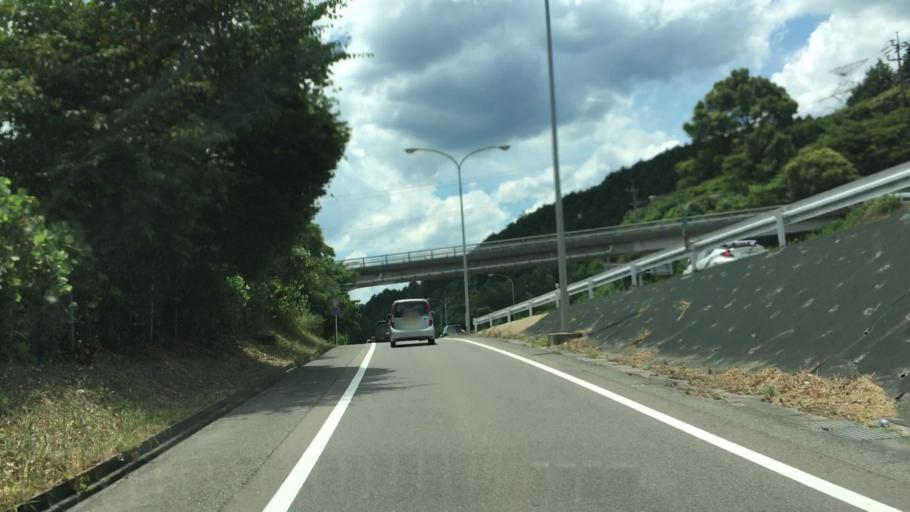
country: JP
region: Fukuoka
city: Chikushino-shi
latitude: 33.4423
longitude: 130.5283
